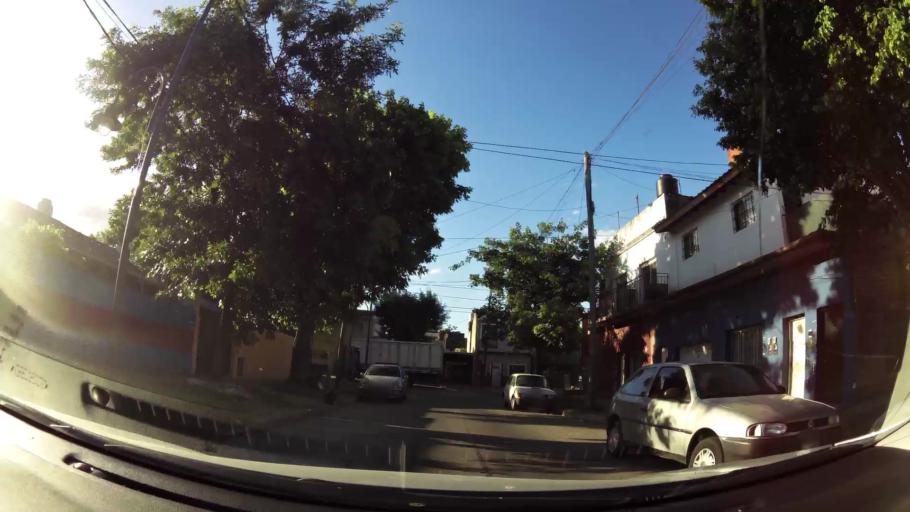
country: AR
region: Buenos Aires
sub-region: Partido de Tigre
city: Tigre
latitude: -34.4630
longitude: -58.5672
